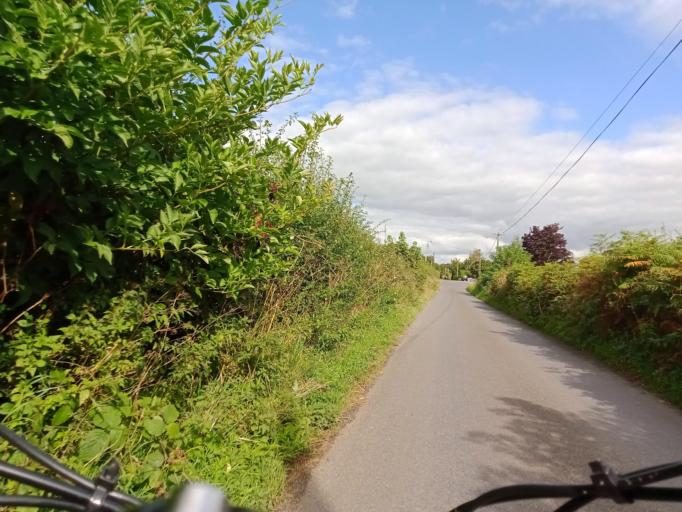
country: IE
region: Leinster
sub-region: Kilkenny
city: Kilkenny
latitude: 52.6046
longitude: -7.2327
